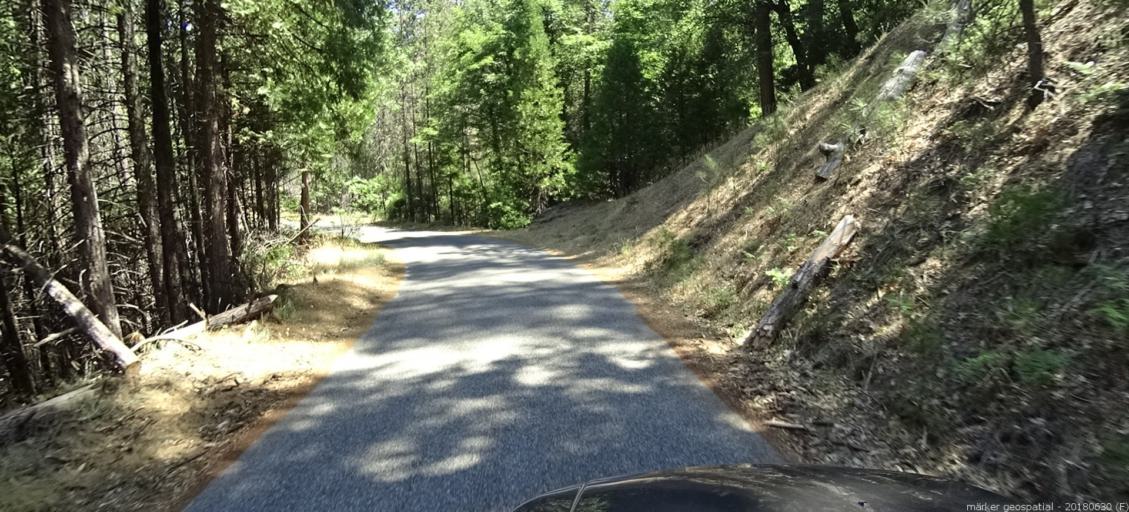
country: US
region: California
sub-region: Madera County
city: Oakhurst
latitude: 37.3644
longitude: -119.3519
